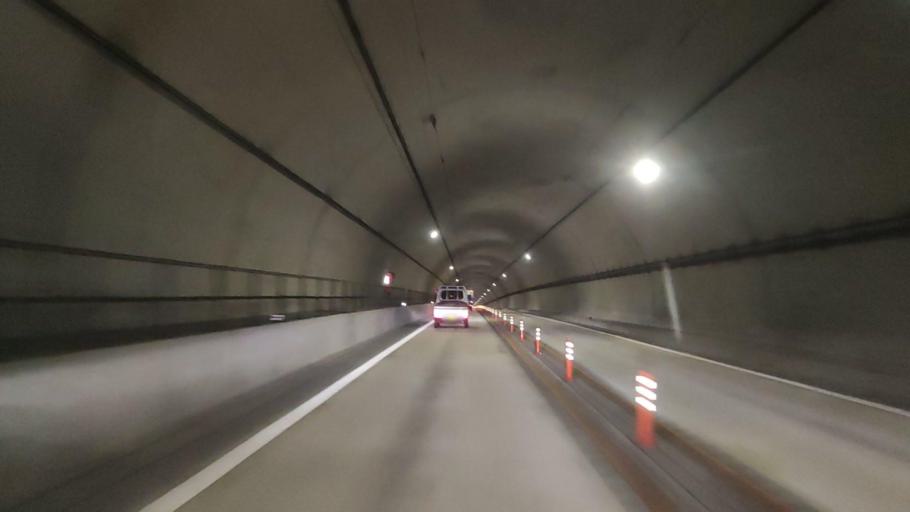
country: JP
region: Wakayama
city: Tanabe
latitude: 33.6048
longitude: 135.4295
